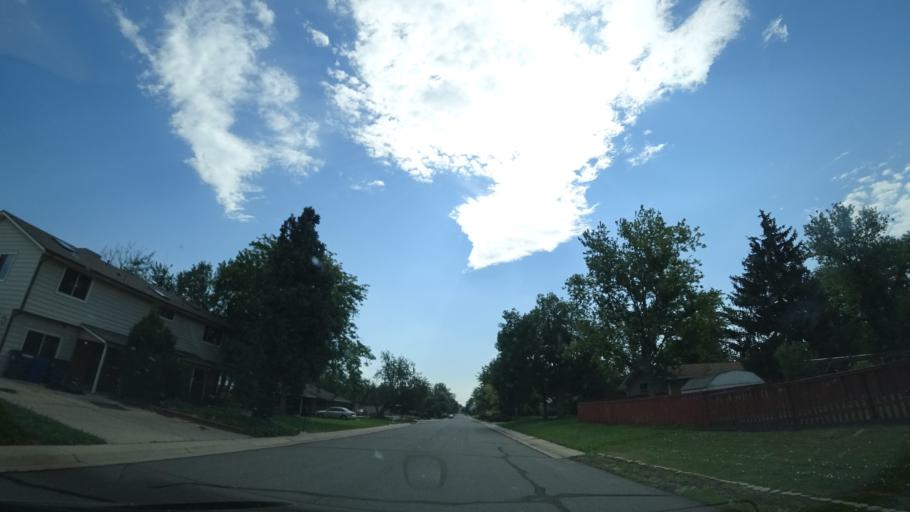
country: US
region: Colorado
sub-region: Jefferson County
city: Lakewood
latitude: 39.7132
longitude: -105.0601
